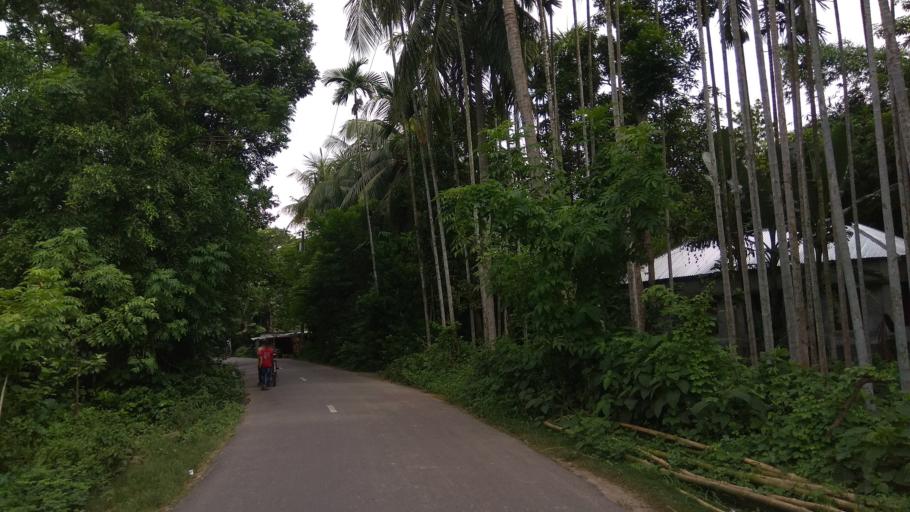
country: BD
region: Khulna
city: Kalia
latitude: 23.1303
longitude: 89.6440
